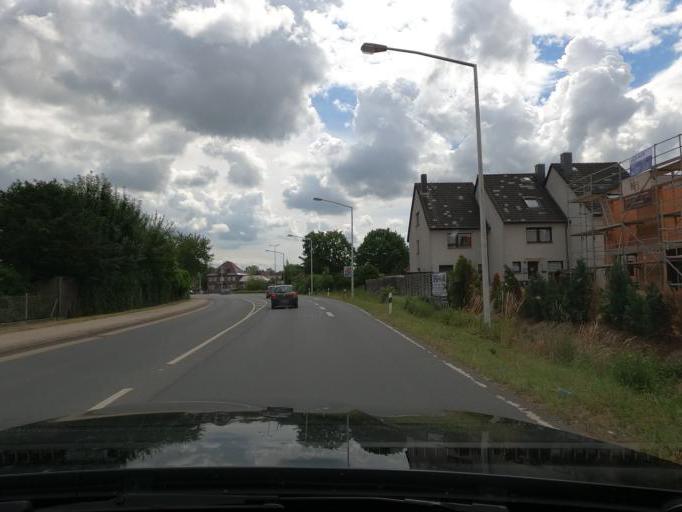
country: DE
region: Lower Saxony
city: Sehnde
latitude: 52.3200
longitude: 9.9556
